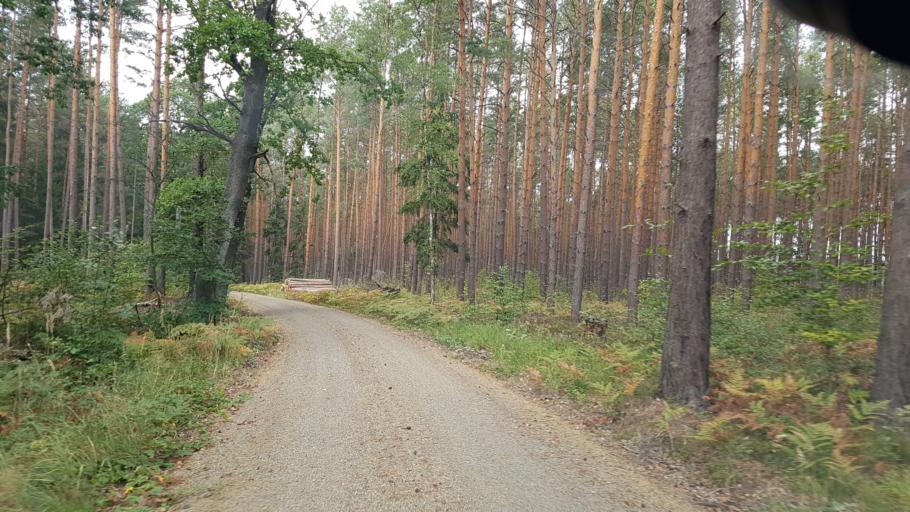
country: DE
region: Brandenburg
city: Ruckersdorf
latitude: 51.5685
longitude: 13.6425
